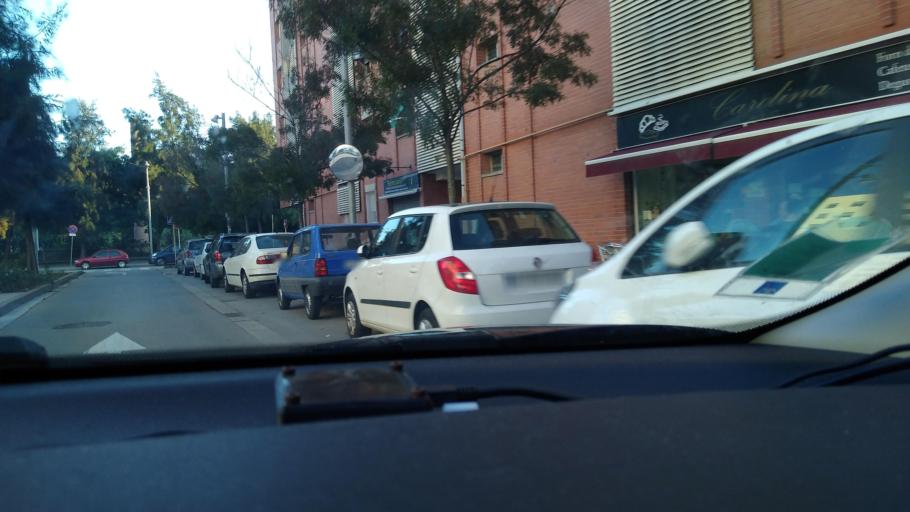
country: ES
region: Catalonia
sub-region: Provincia de Barcelona
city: Sant Joan Despi
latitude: 41.3604
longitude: 2.0605
